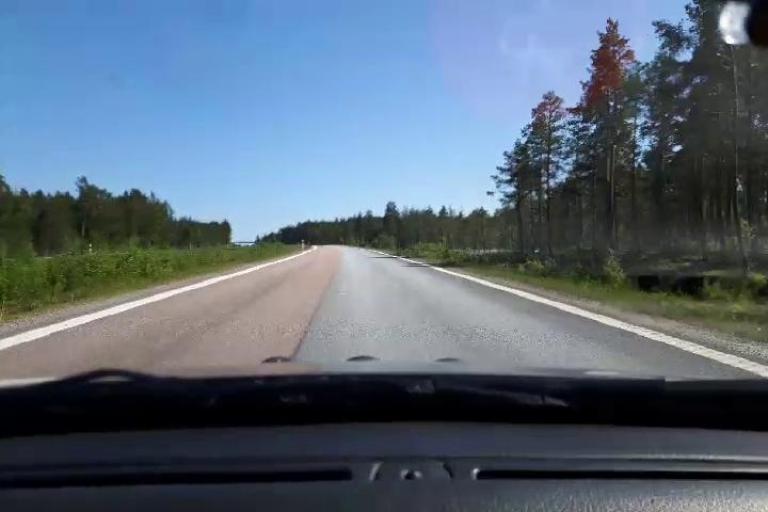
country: SE
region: Gaevleborg
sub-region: Soderhamns Kommun
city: Soderhamn
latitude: 61.3771
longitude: 16.9960
